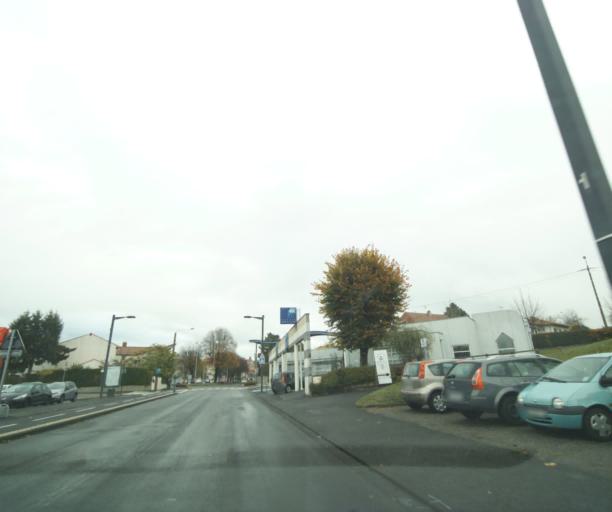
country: FR
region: Auvergne
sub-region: Departement du Puy-de-Dome
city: Cournon-d'Auvergne
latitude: 45.7378
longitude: 3.1951
